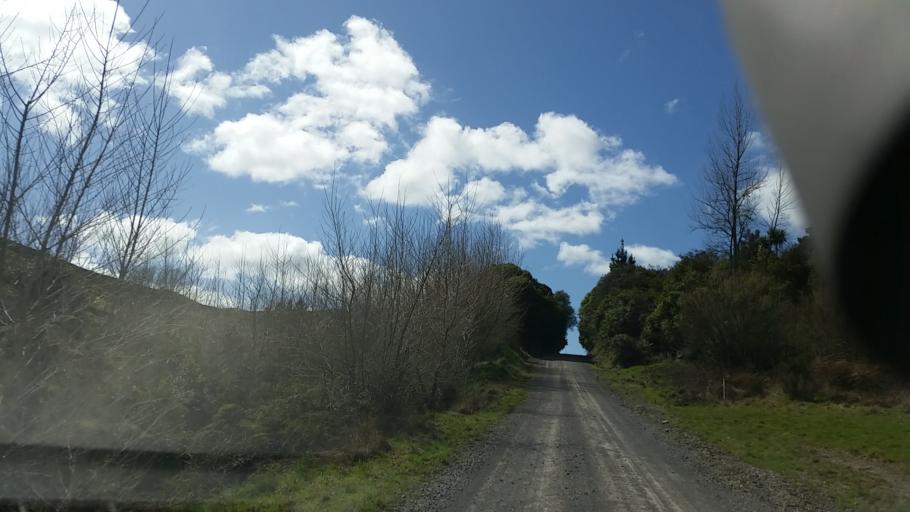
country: NZ
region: Waikato
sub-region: Taupo District
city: Taupo
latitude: -38.4860
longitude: 176.2103
